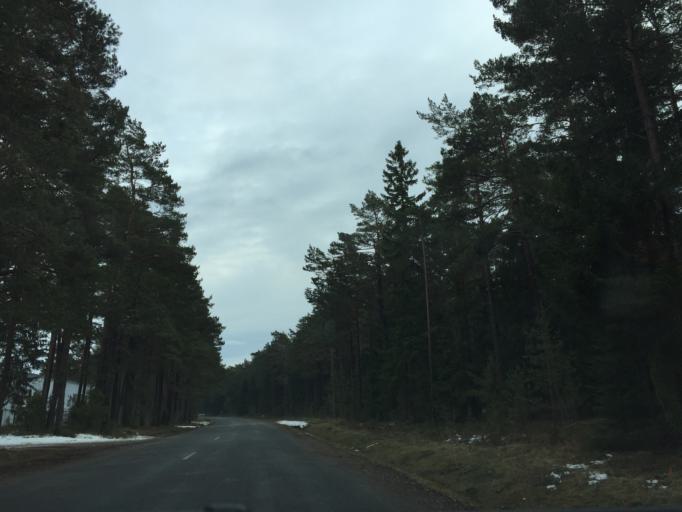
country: EE
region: Saare
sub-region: Kuressaare linn
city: Kuressaare
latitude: 58.4393
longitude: 22.0597
